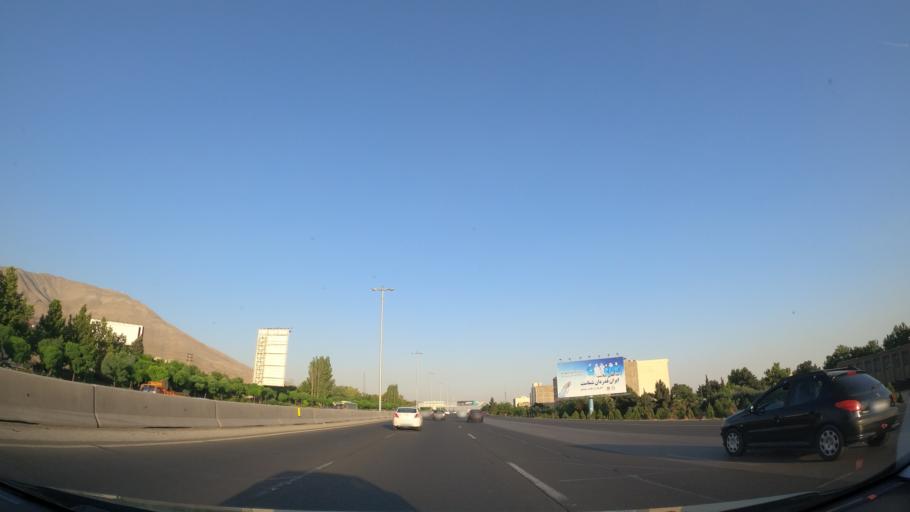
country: IR
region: Alborz
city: Karaj
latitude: 35.7847
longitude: 51.0280
